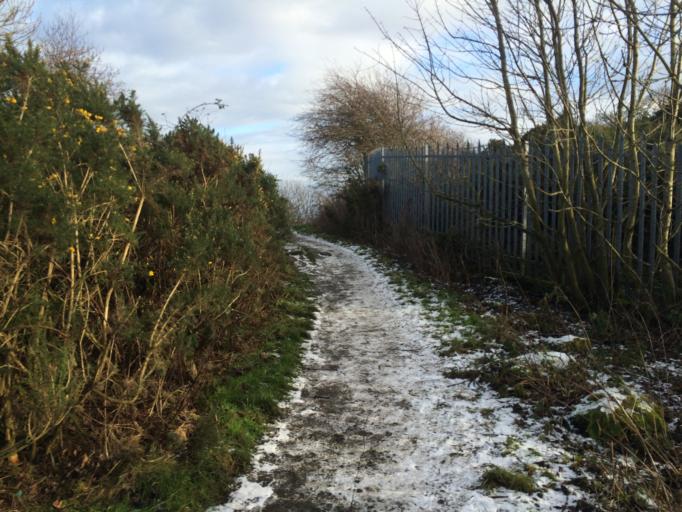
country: GB
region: Scotland
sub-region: Edinburgh
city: Colinton
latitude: 55.9483
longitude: -3.2647
